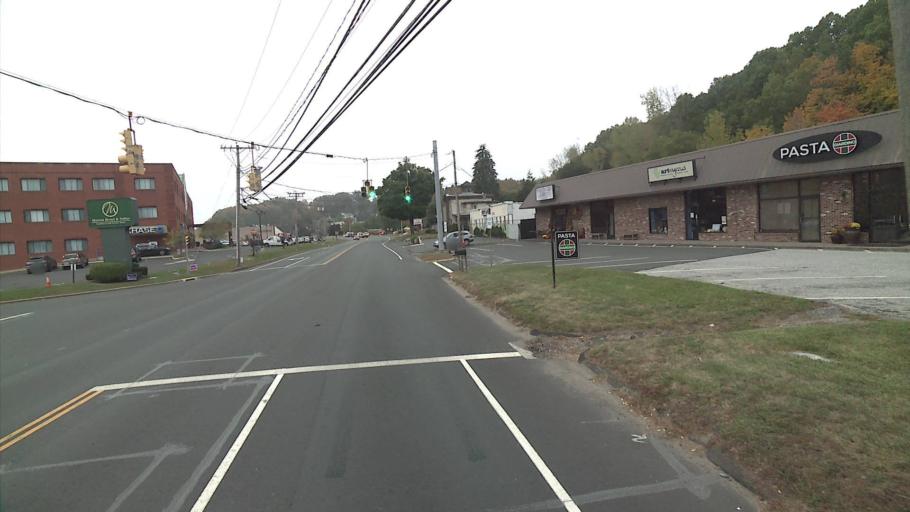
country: US
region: Connecticut
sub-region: Fairfield County
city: Danbury
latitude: 41.3854
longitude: -73.4852
